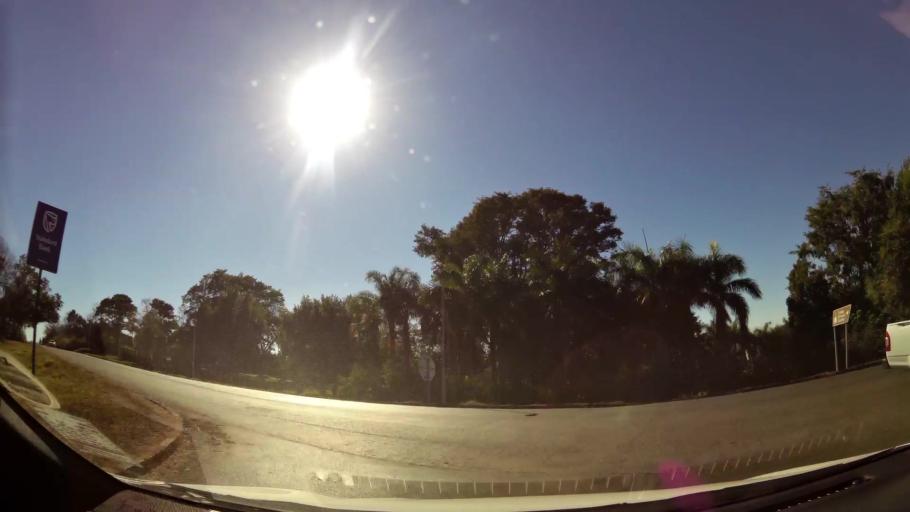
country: ZA
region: Limpopo
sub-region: Mopani District Municipality
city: Tzaneen
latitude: -23.8446
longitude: 30.1672
